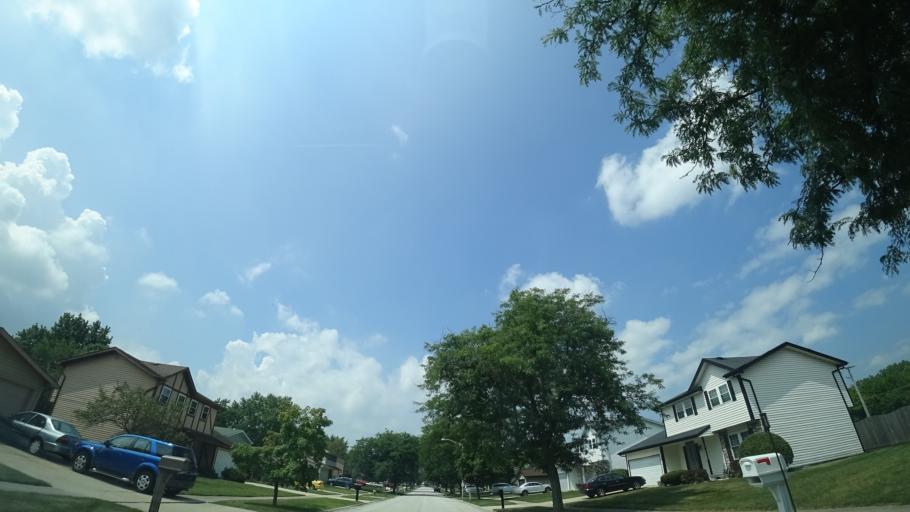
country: US
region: Illinois
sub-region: Will County
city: Frankfort Square
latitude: 41.5266
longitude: -87.7570
